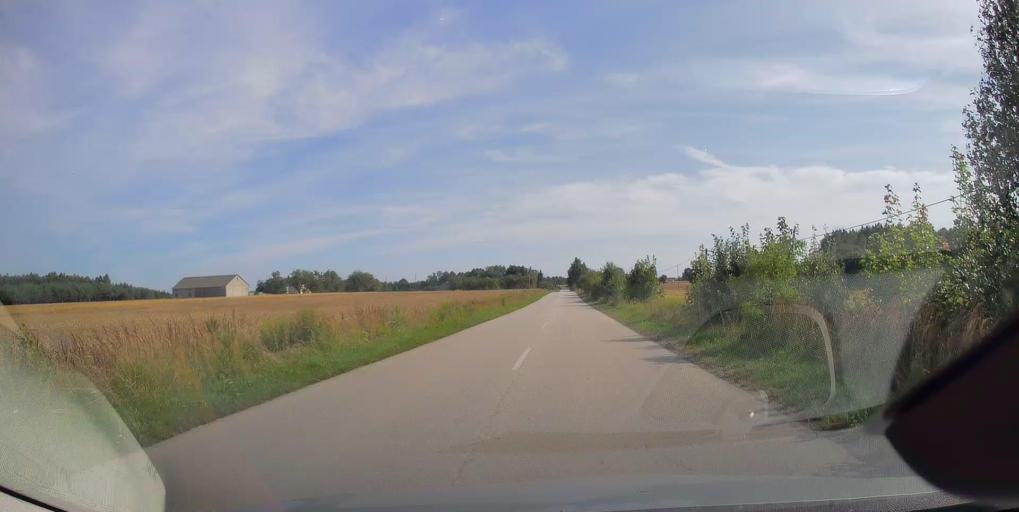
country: PL
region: Lodz Voivodeship
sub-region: Powiat opoczynski
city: Mniszkow
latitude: 51.3597
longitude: 20.0372
